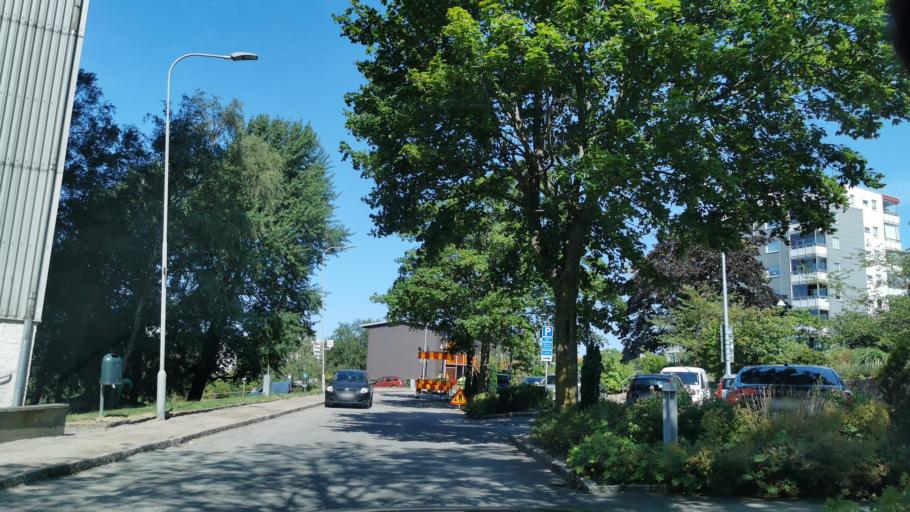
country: SE
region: Vaestra Goetaland
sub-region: Goteborg
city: Majorna
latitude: 57.6514
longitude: 11.9187
